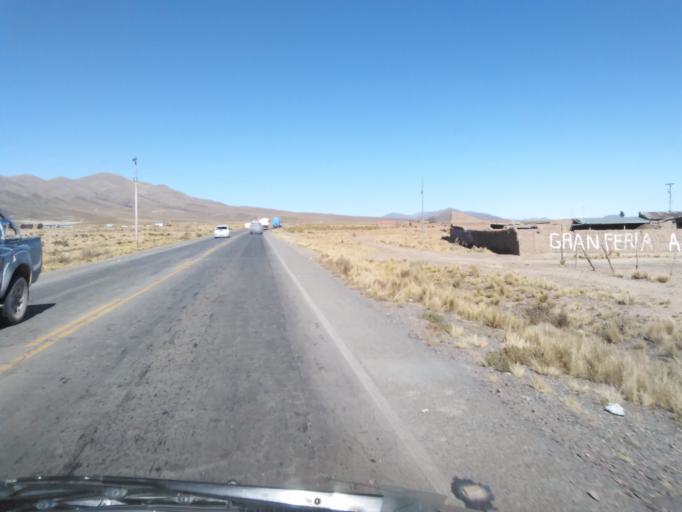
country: BO
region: Oruro
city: Machacamarca
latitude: -18.0552
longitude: -67.0077
